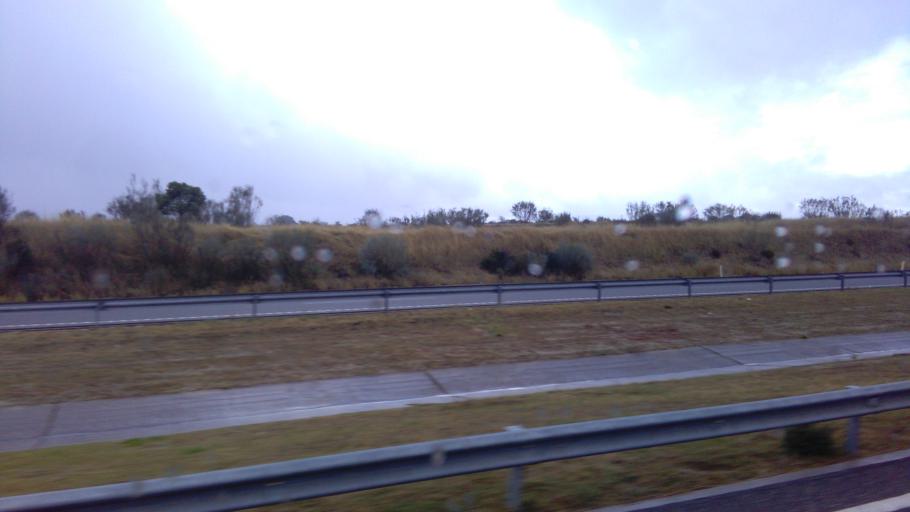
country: ES
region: Madrid
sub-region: Provincia de Madrid
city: Arroyomolinos
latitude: 40.2614
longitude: -3.9626
